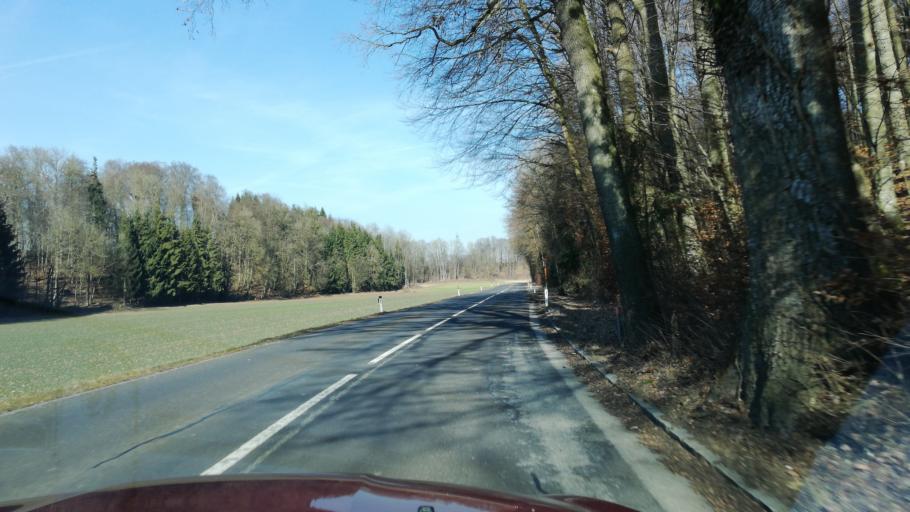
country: AT
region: Upper Austria
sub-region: Politischer Bezirk Vocklabruck
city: Desselbrunn
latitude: 48.0292
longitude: 13.7742
